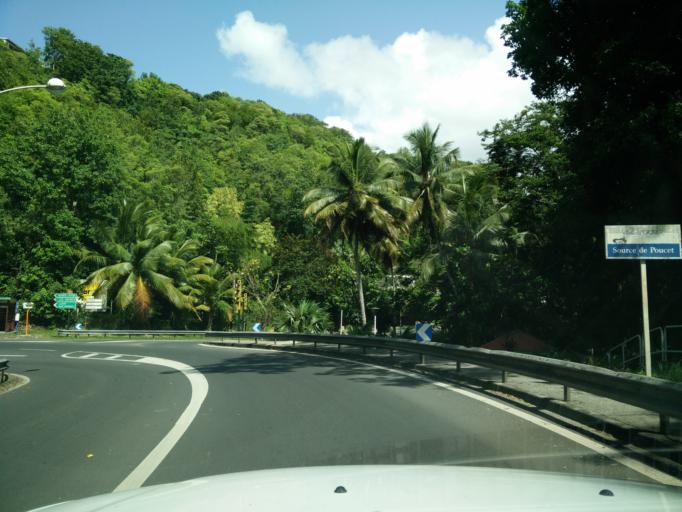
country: GP
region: Guadeloupe
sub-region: Guadeloupe
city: Le Gosier
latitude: 16.2191
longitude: -61.5050
